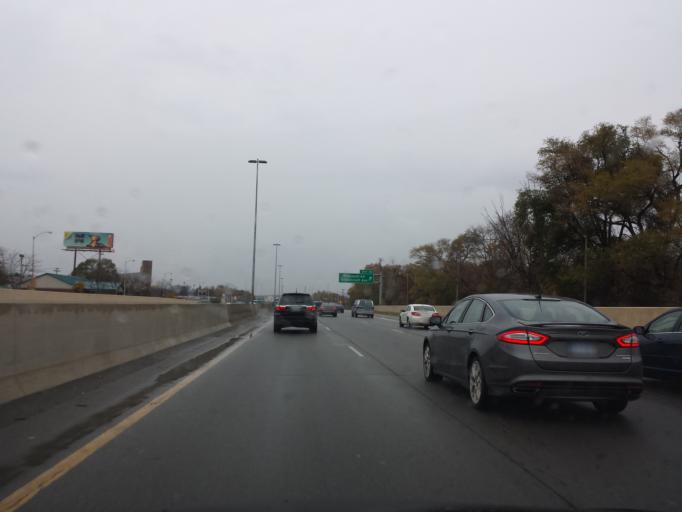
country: US
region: Michigan
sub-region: Wayne County
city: Dearborn
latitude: 42.3679
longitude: -83.2165
